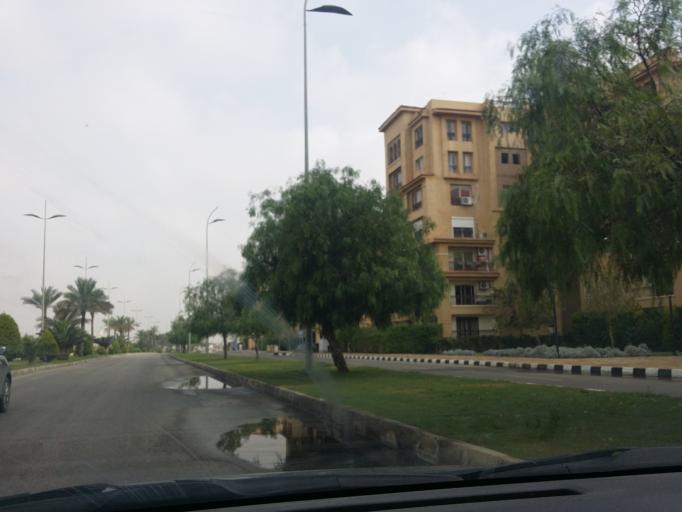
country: EG
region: Muhafazat al Qalyubiyah
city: Al Khankah
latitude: 30.1027
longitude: 31.6328
